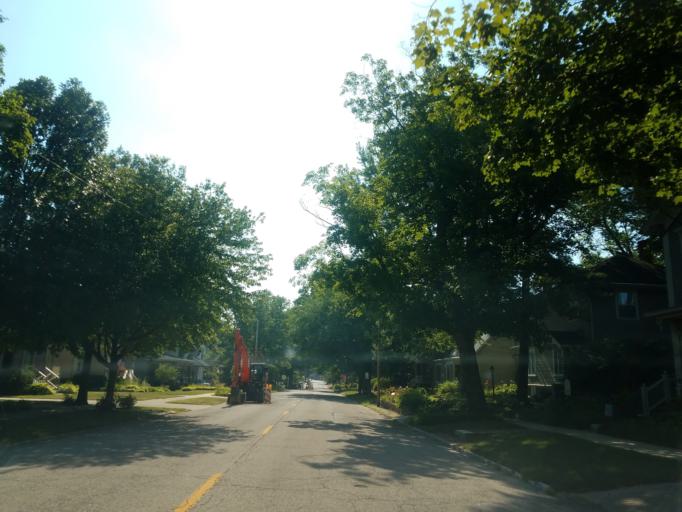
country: US
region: Illinois
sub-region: McLean County
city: Bloomington
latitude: 40.4780
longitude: -88.9872
